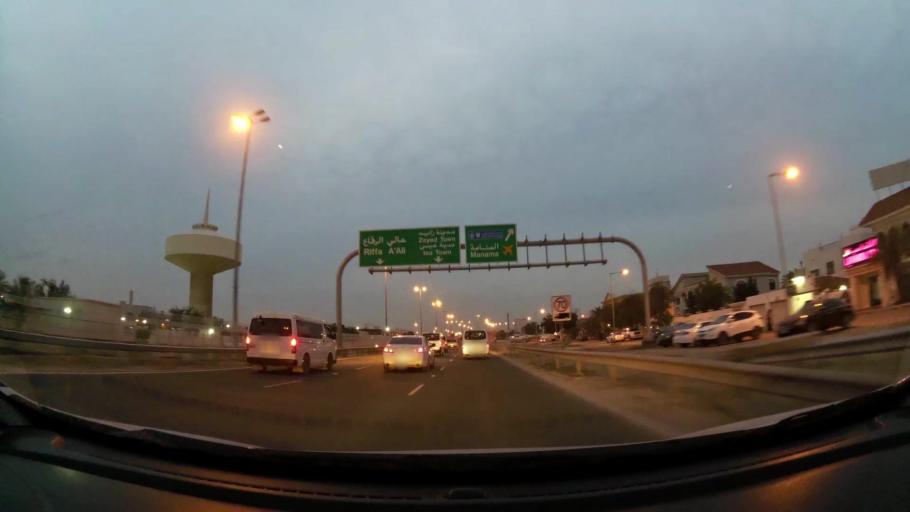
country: BH
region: Northern
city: Madinat `Isa
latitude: 26.1665
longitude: 50.5495
